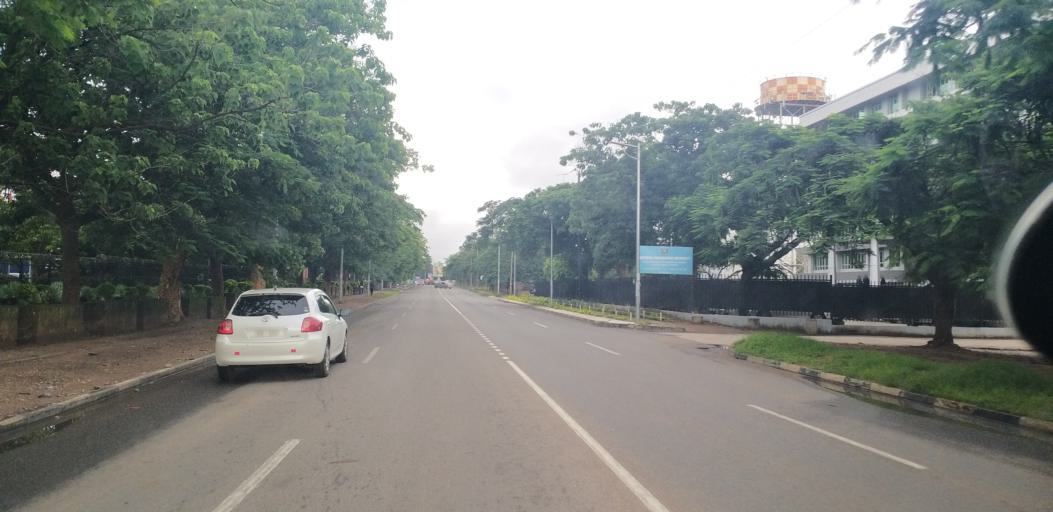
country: ZM
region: Lusaka
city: Lusaka
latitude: -15.4231
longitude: 28.3095
